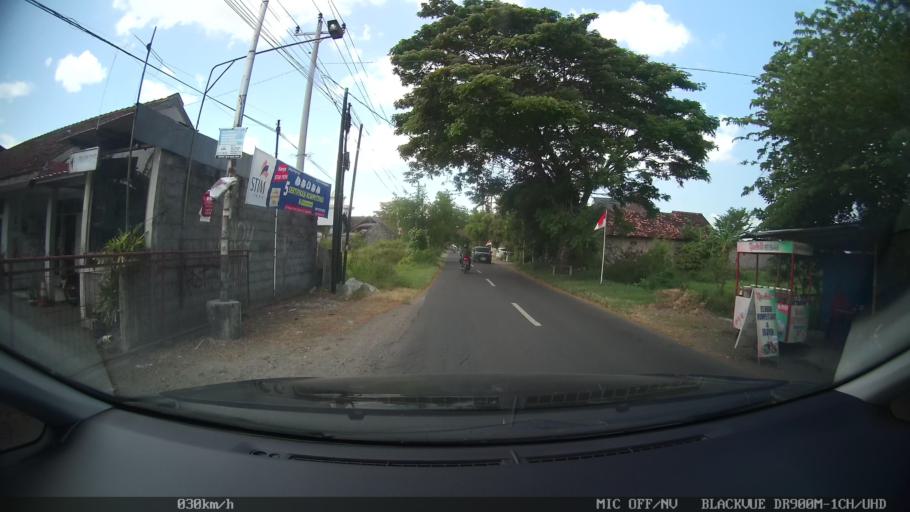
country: ID
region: Daerah Istimewa Yogyakarta
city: Sewon
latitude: -7.8701
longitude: 110.3546
